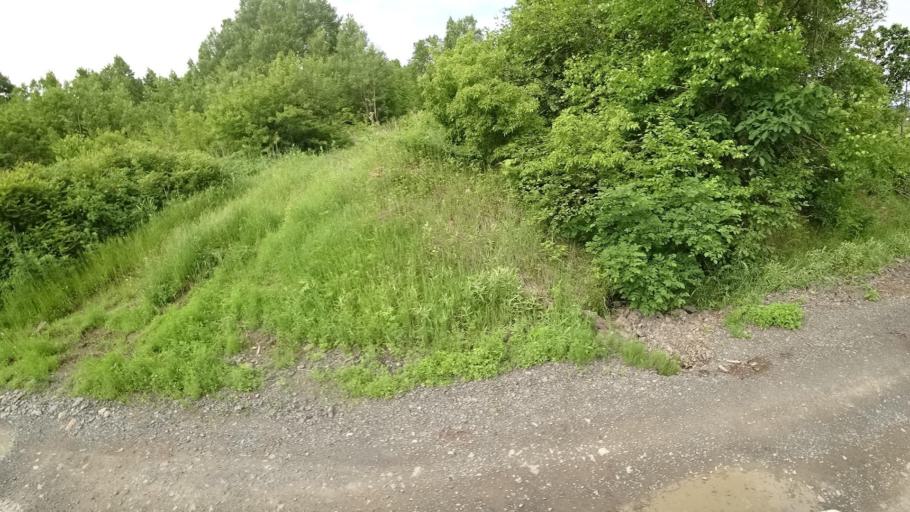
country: RU
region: Khabarovsk Krai
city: Amursk
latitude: 49.9004
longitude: 136.1496
